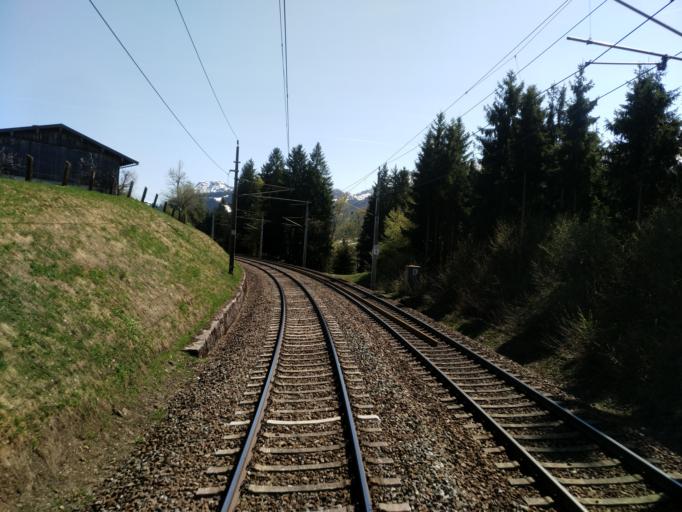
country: AT
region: Tyrol
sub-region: Politischer Bezirk Kitzbuhel
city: Fieberbrunn
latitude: 47.4819
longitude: 12.5398
